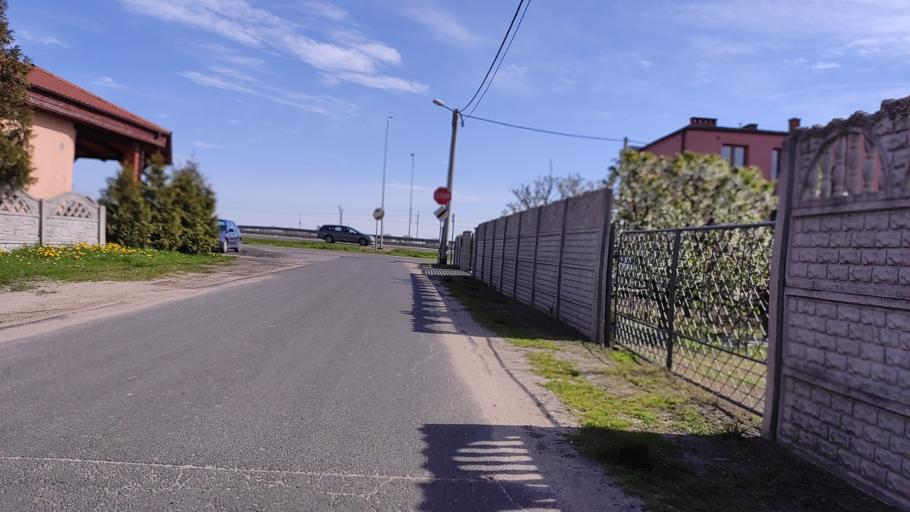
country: PL
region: Greater Poland Voivodeship
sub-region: Powiat poznanski
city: Kostrzyn
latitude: 52.3966
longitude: 17.1780
